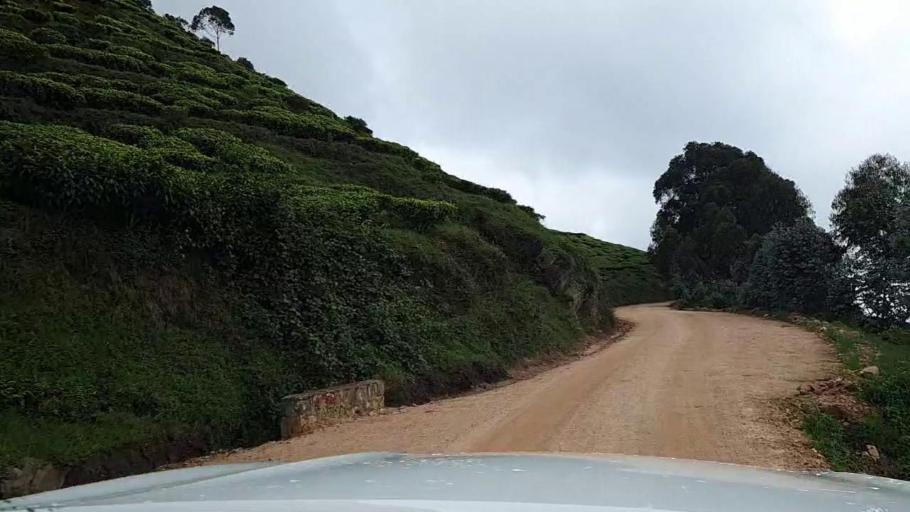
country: RW
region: Western Province
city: Kibuye
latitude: -2.2977
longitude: 29.3826
